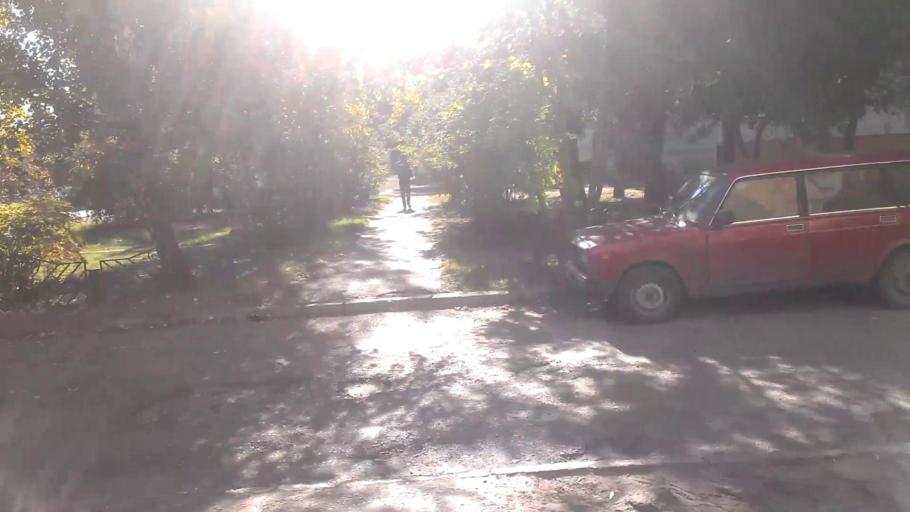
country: RU
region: Altai Krai
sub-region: Gorod Barnaulskiy
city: Barnaul
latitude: 53.3723
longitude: 83.6909
